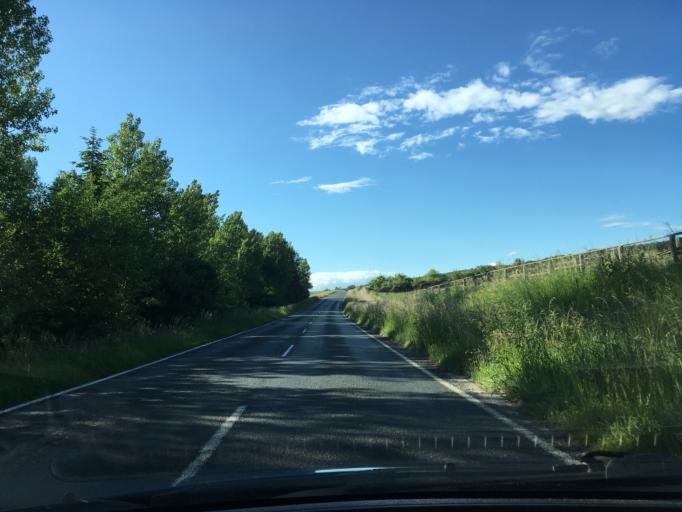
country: DE
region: Lower Saxony
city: Duingen
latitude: 51.9968
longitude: 9.7118
